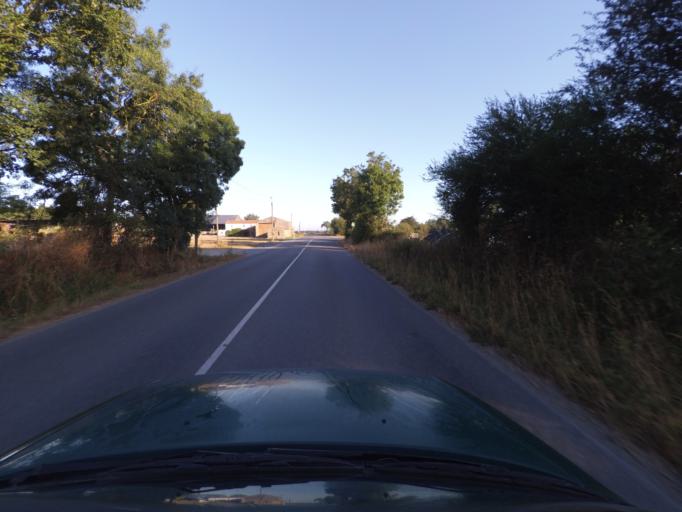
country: FR
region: Pays de la Loire
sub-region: Departement de la Loire-Atlantique
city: La Planche
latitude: 46.9958
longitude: -1.4534
